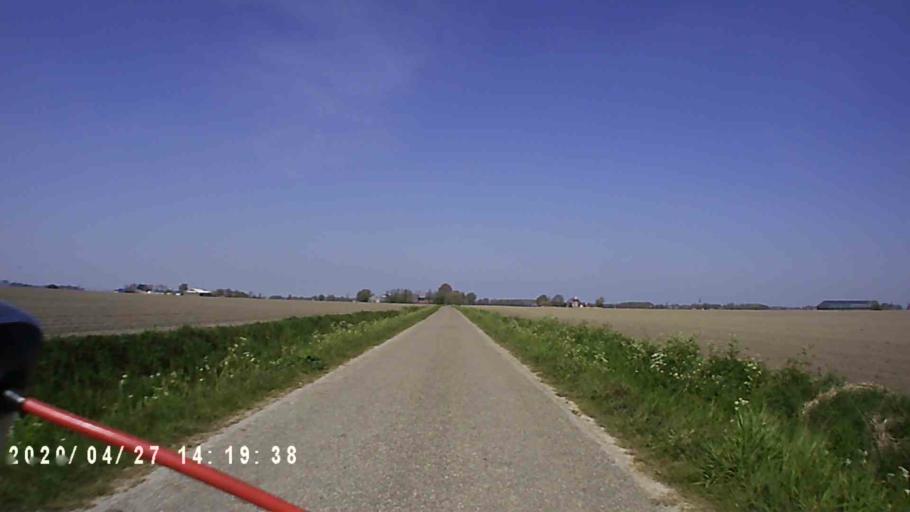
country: NL
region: Groningen
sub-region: Gemeente De Marne
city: Ulrum
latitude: 53.3670
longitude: 6.3849
